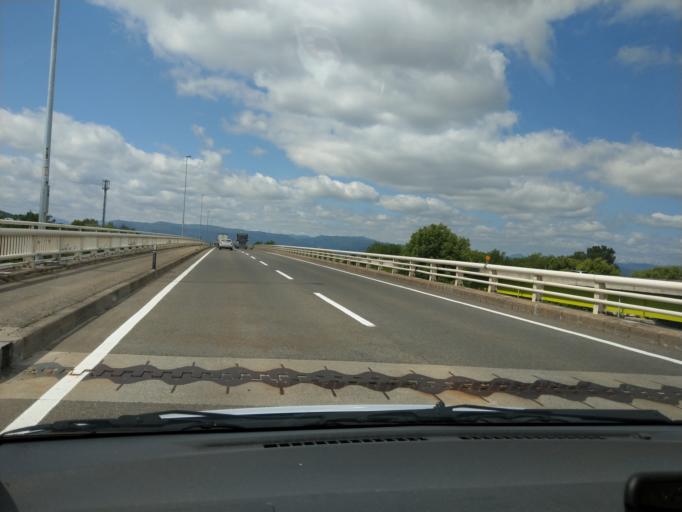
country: JP
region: Akita
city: Yuzawa
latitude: 39.2107
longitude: 140.5117
